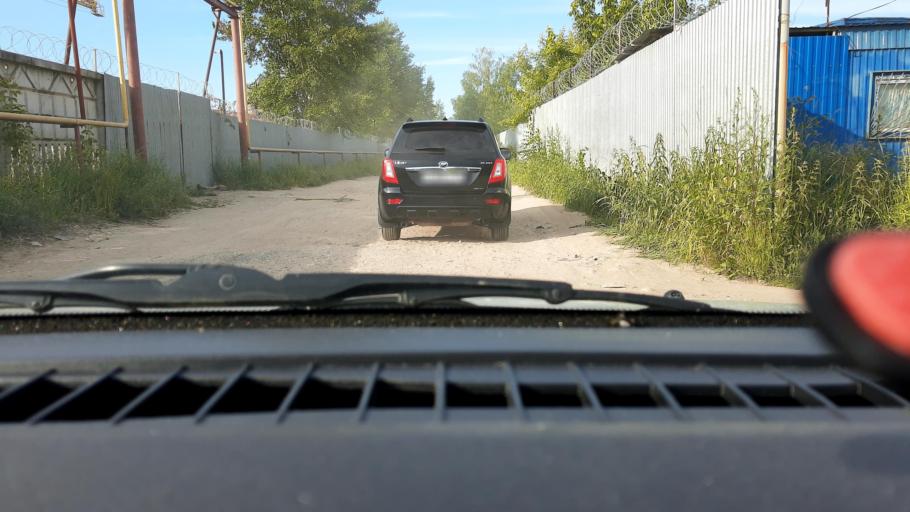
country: RU
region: Nizjnij Novgorod
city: Kstovo
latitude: 56.1226
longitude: 44.1364
